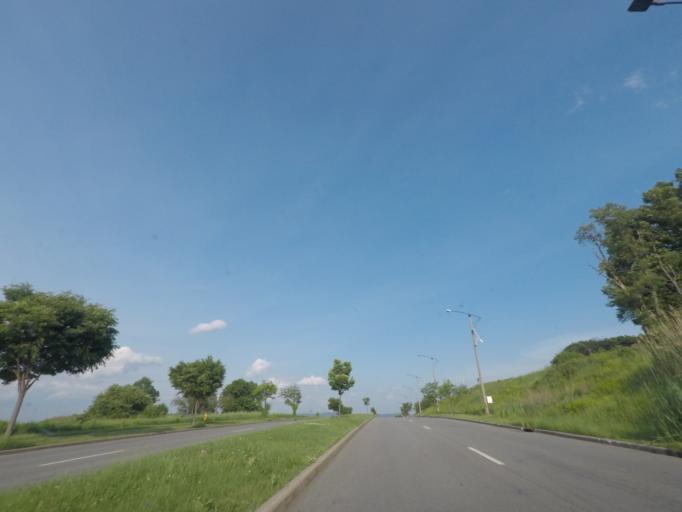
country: US
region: New York
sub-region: Orange County
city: Orange Lake
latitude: 41.4964
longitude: -74.1084
